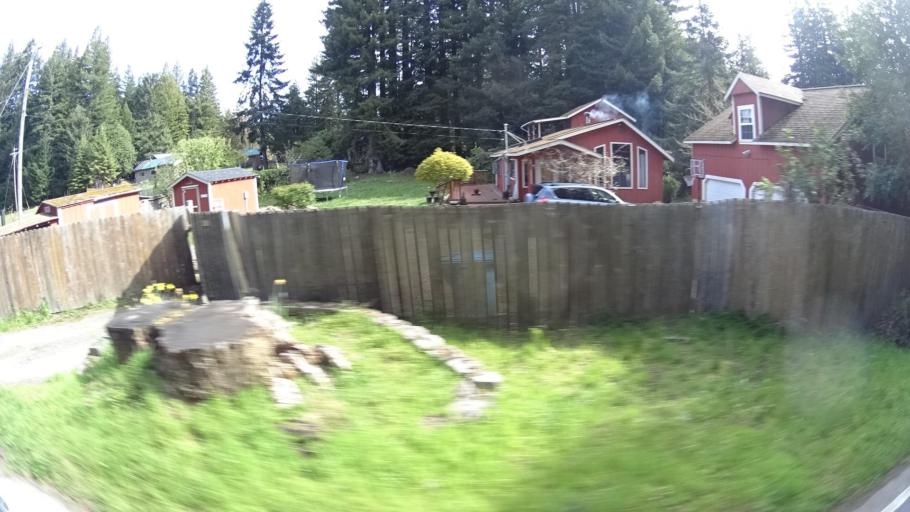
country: US
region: California
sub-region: Humboldt County
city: Bayside
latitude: 40.7570
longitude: -123.9901
